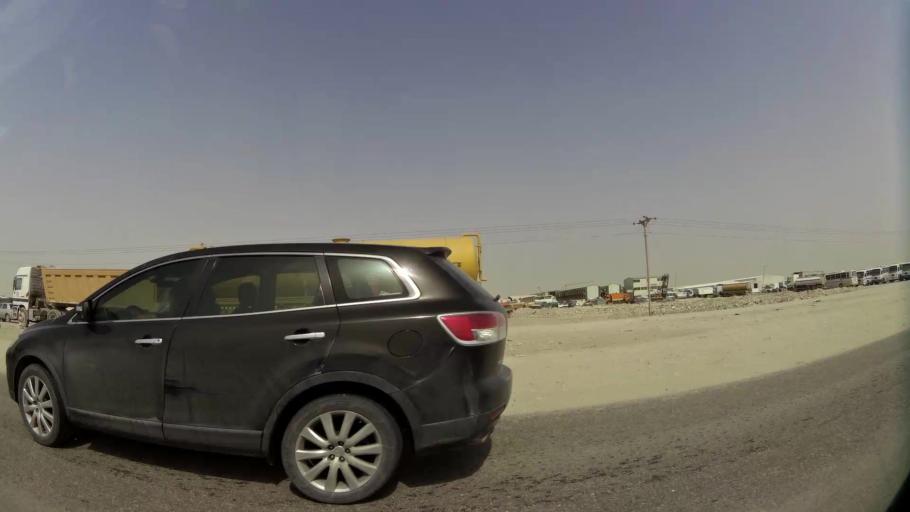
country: QA
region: Baladiyat ar Rayyan
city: Ar Rayyan
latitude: 25.2019
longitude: 51.3649
